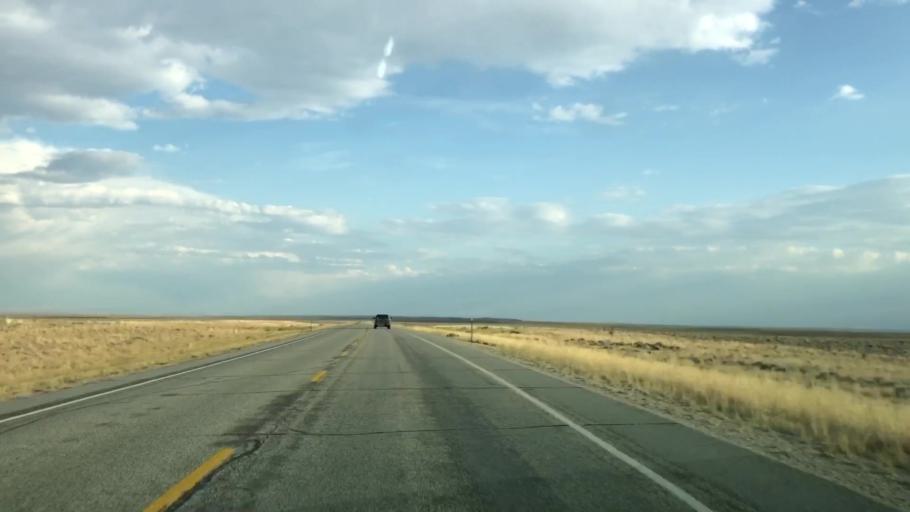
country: US
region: Wyoming
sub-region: Sublette County
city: Marbleton
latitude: 42.3361
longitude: -109.5198
